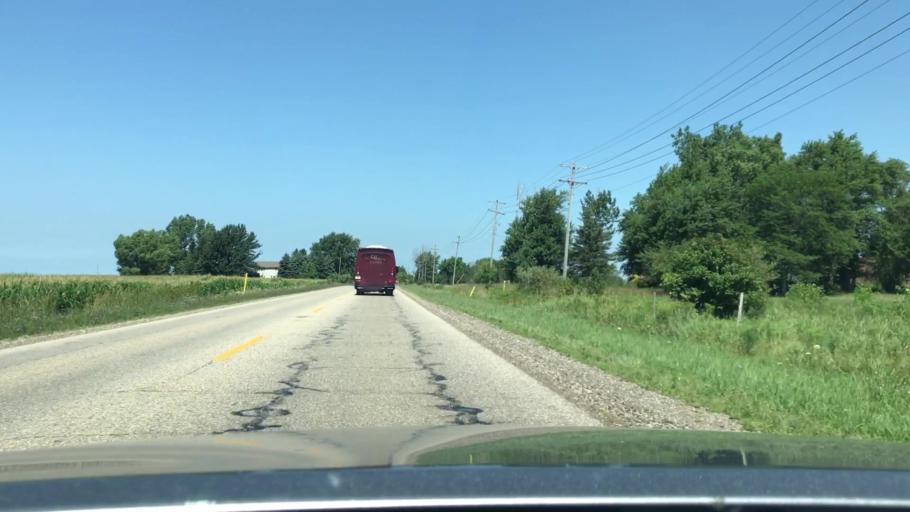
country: US
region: Michigan
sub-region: Ottawa County
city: Zeeland
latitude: 42.8634
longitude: -86.0796
